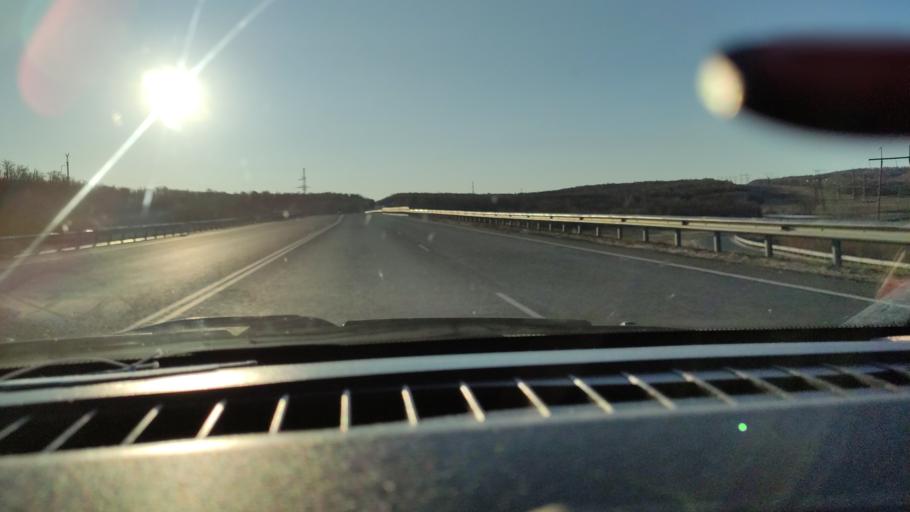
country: RU
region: Saratov
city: Vol'sk
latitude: 52.1144
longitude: 47.3051
